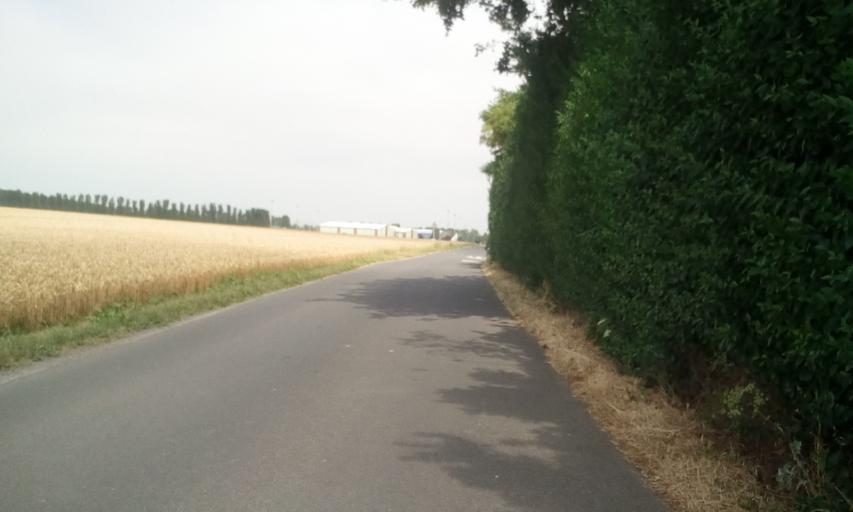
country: FR
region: Lower Normandy
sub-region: Departement du Calvados
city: Douvres-la-Delivrande
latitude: 49.2937
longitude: -0.3927
